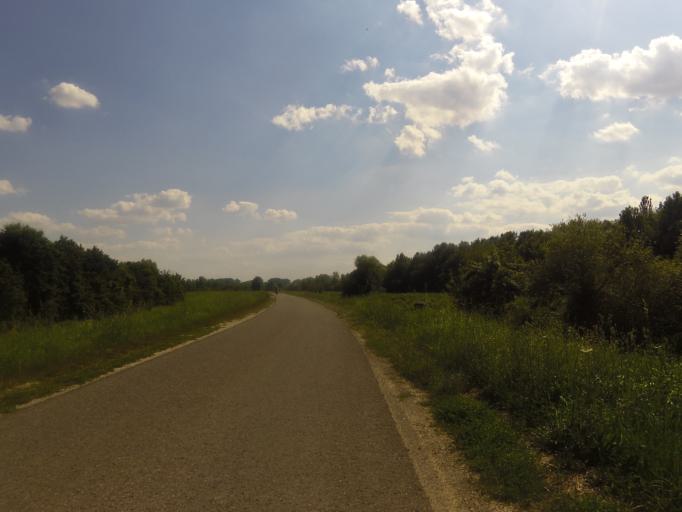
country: HU
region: Jasz-Nagykun-Szolnok
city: Tiszaszolos
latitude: 47.6019
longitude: 20.7085
